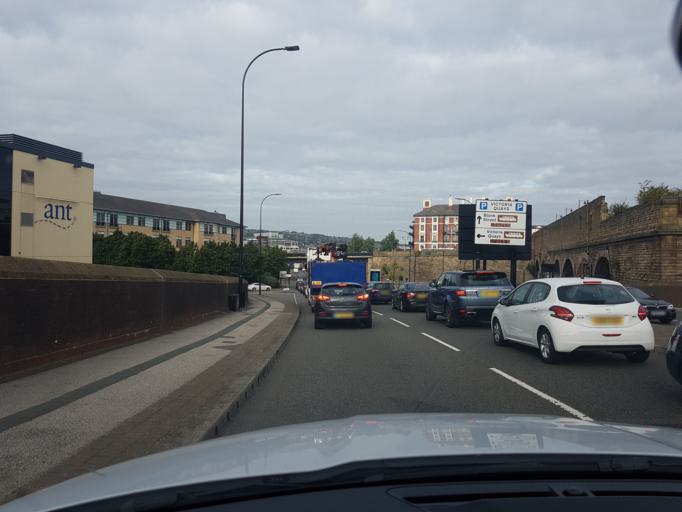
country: GB
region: England
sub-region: Sheffield
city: Sheffield
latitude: 53.3864
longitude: -1.4569
